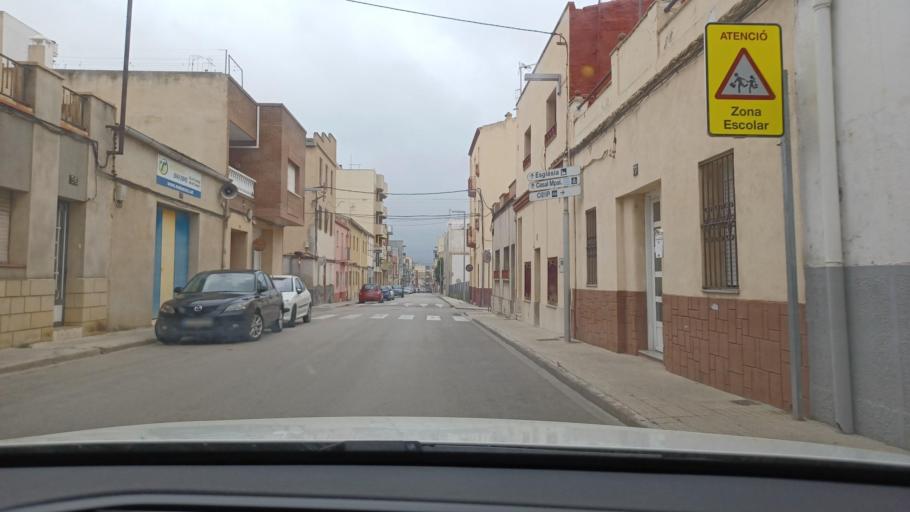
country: ES
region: Catalonia
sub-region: Provincia de Tarragona
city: Tortosa
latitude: 40.8080
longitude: 0.4928
